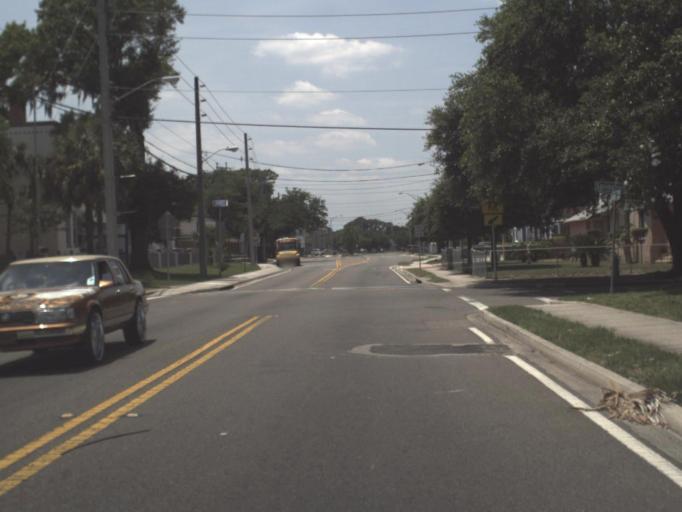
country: US
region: Florida
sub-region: Duval County
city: Jacksonville
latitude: 30.3628
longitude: -81.6621
